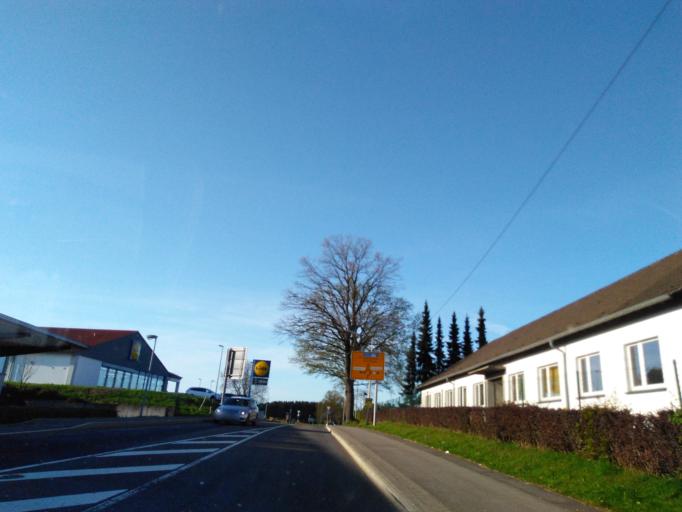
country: DE
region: North Rhine-Westphalia
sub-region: Regierungsbezirk Koln
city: Much
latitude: 50.9463
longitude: 7.4536
